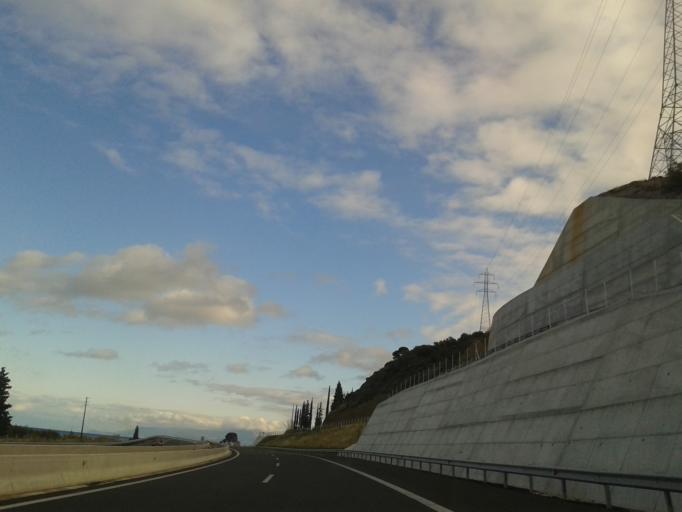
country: GR
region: Peloponnese
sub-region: Nomos Korinthias
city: Xylokastro
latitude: 38.0945
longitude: 22.5647
